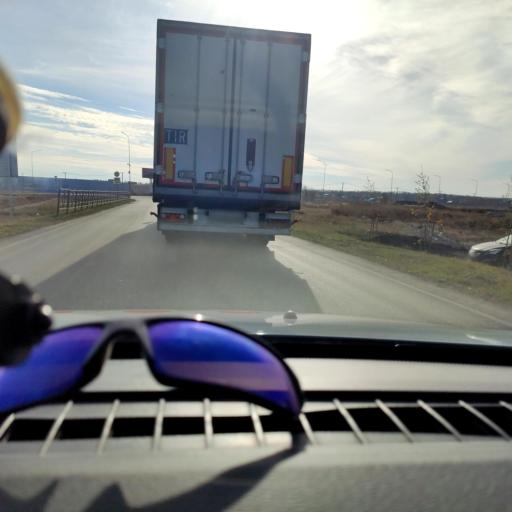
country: RU
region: Samara
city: Samara
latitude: 53.0919
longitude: 50.1346
